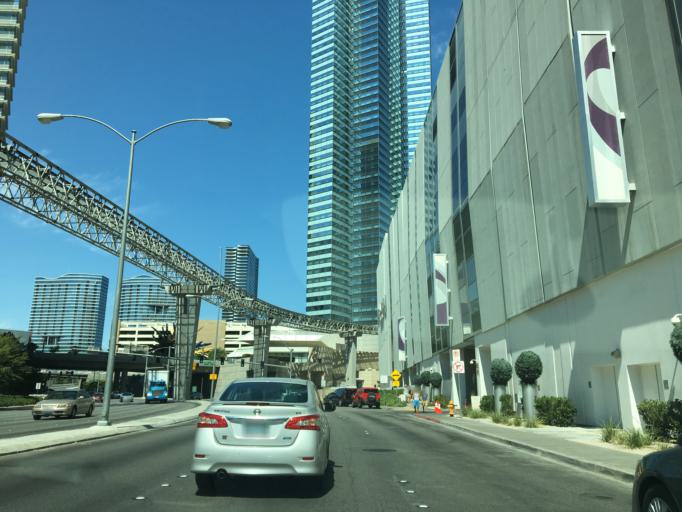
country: US
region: Nevada
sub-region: Clark County
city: Paradise
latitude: 36.1093
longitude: -115.1753
